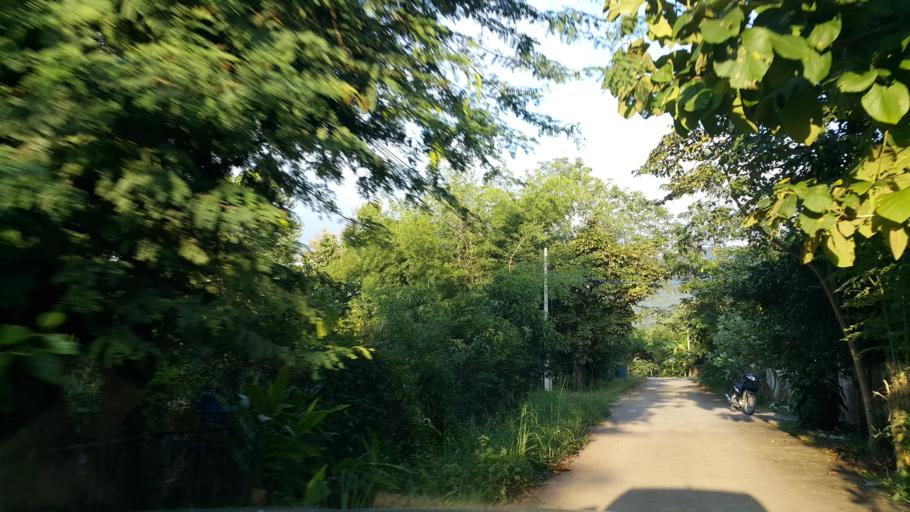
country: TH
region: Chiang Mai
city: Mae On
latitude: 18.7452
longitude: 99.2561
